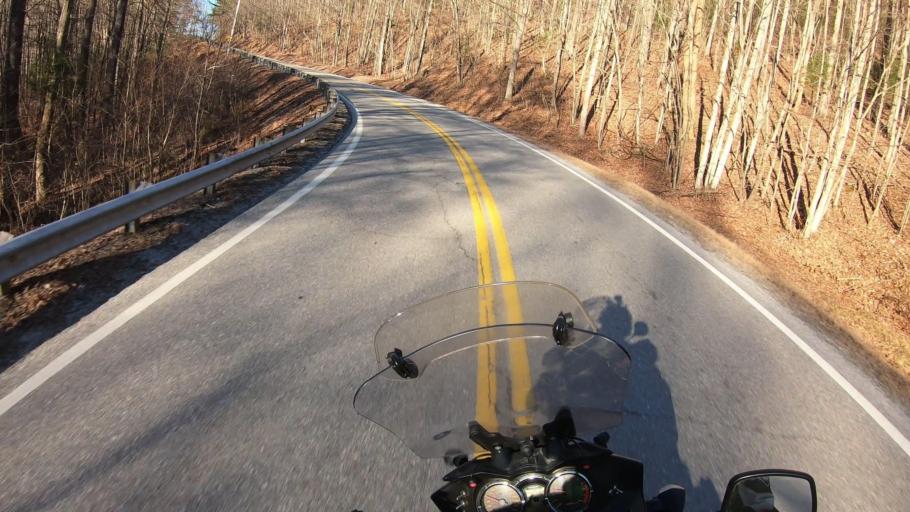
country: US
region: Georgia
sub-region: Lumpkin County
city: Dahlonega
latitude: 34.6886
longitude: -84.0121
